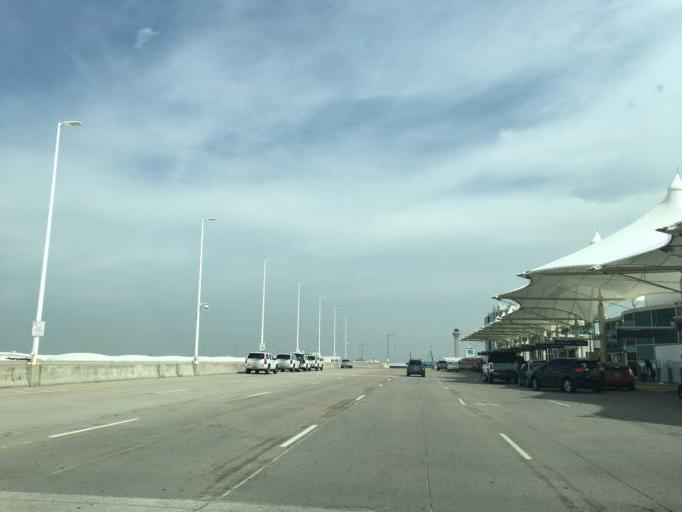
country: US
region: Colorado
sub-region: Weld County
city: Lochbuie
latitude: 39.8493
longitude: -104.6750
